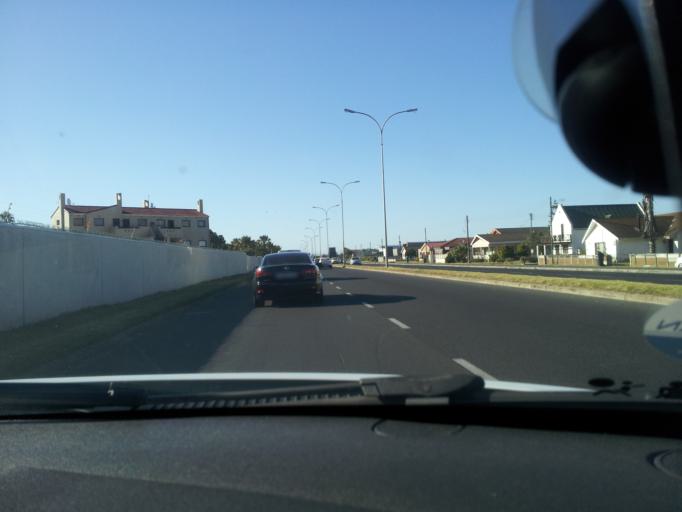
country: ZA
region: Western Cape
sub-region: Overberg District Municipality
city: Grabouw
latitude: -34.1339
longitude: 18.8457
